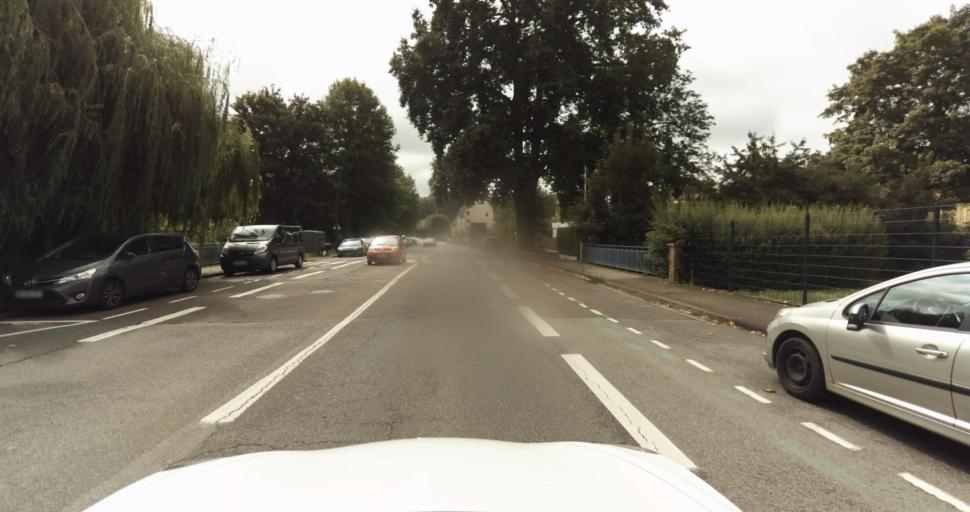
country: FR
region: Haute-Normandie
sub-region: Departement de l'Eure
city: Evreux
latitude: 49.0257
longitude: 1.1384
